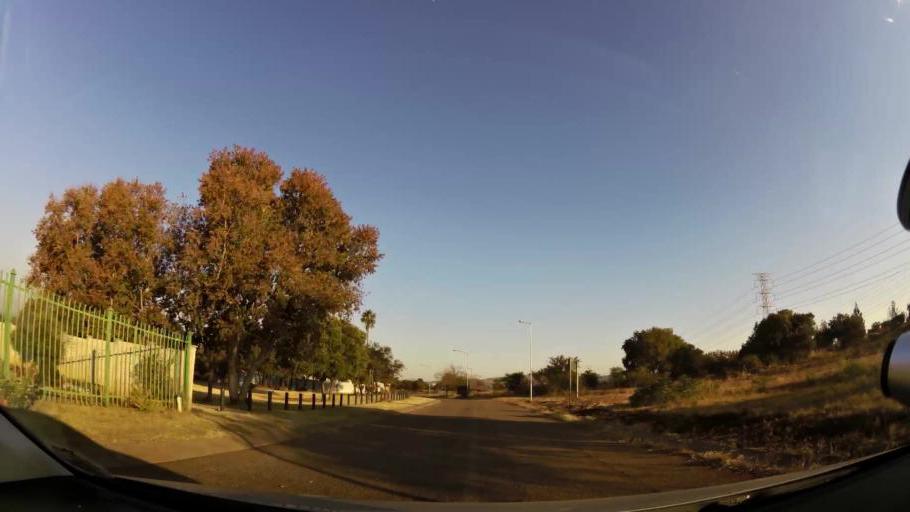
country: ZA
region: Gauteng
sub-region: City of Tshwane Metropolitan Municipality
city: Pretoria
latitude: -25.7401
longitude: 28.1069
